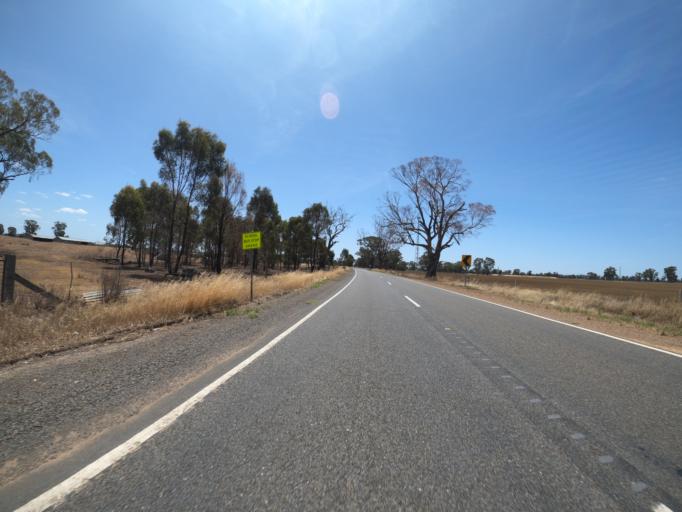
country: AU
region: Victoria
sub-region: Moira
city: Yarrawonga
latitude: -36.1898
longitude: 145.9672
